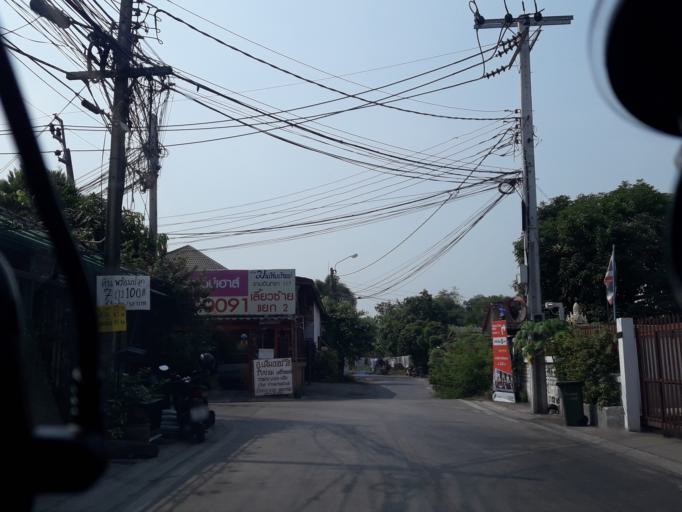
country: TH
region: Bangkok
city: Khan Na Yao
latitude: 13.8187
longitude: 100.7040
